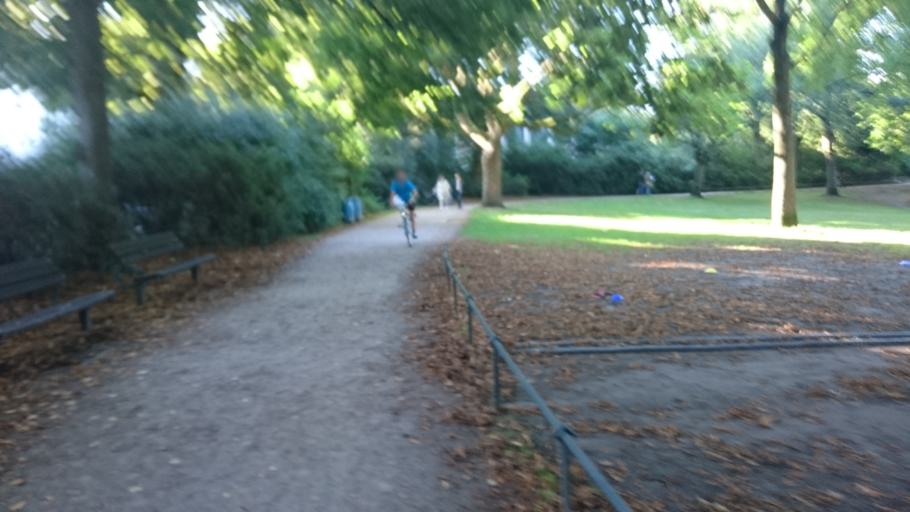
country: DE
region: Hamburg
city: St. Pauli
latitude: 53.5766
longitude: 9.9605
